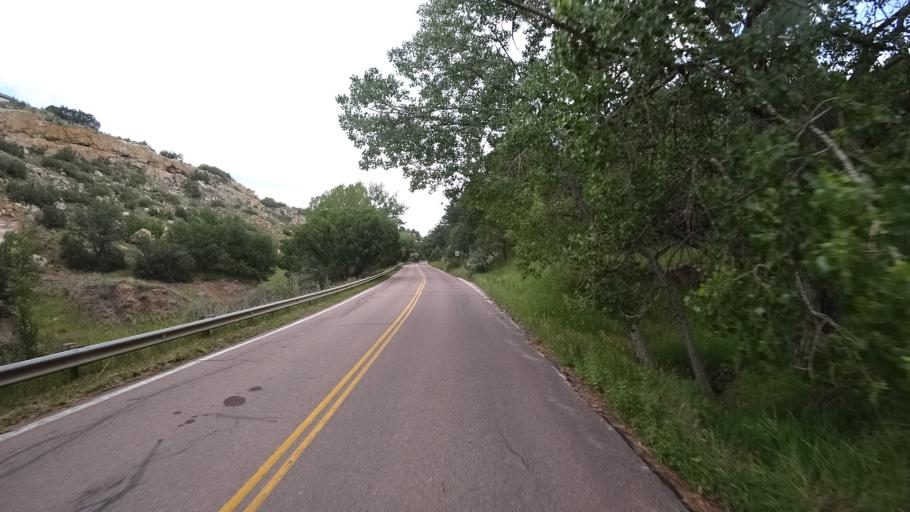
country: US
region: Colorado
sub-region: El Paso County
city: Colorado Springs
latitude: 38.9070
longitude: -104.8344
